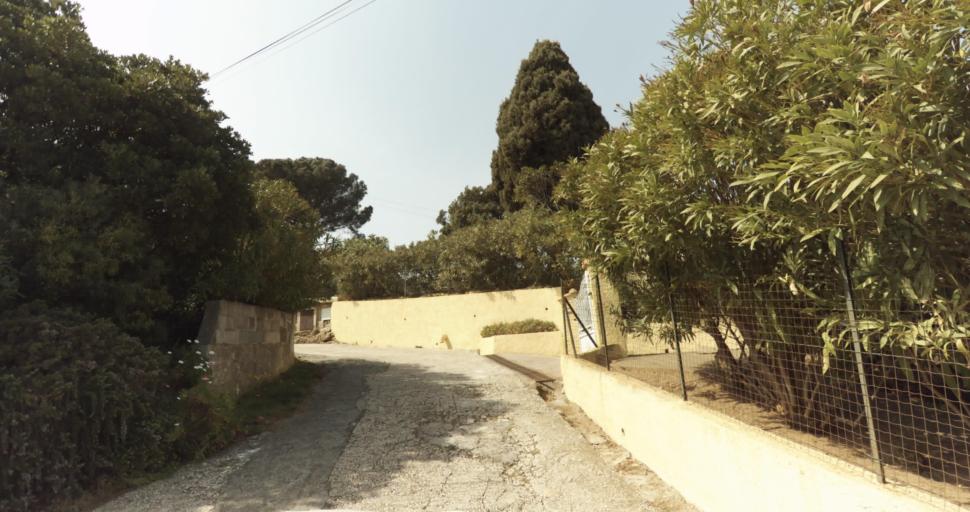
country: FR
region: Provence-Alpes-Cote d'Azur
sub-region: Departement du Var
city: Bormes-les-Mimosas
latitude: 43.1508
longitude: 6.3480
